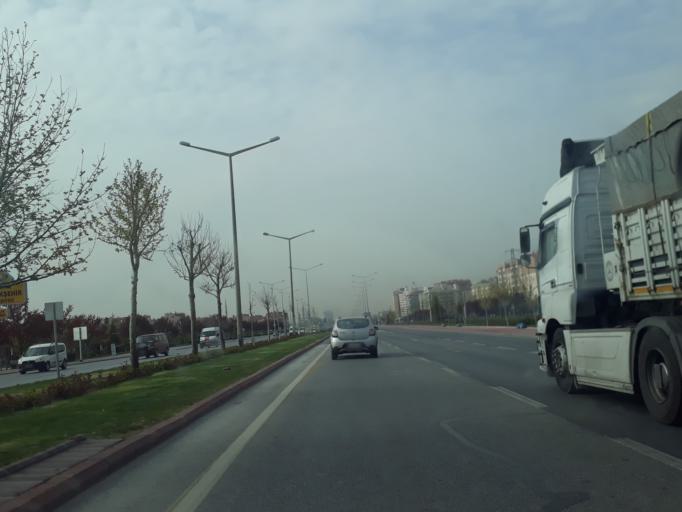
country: TR
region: Konya
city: Selcuklu
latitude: 37.9628
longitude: 32.5146
